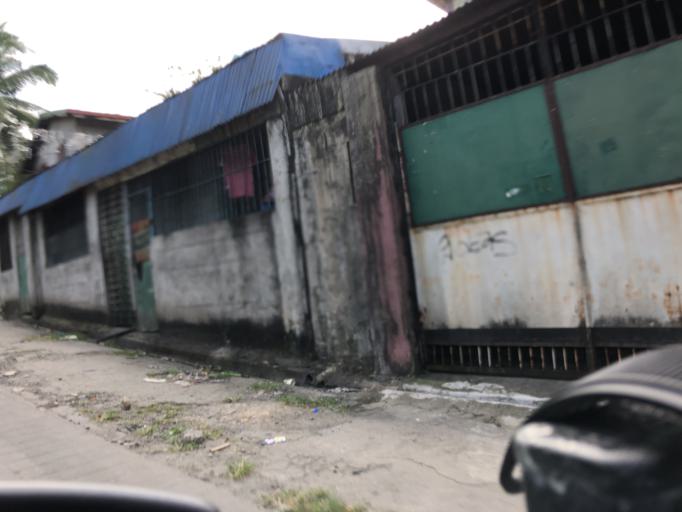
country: PH
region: Central Luzon
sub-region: Province of Bulacan
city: San Jose del Monte
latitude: 14.7428
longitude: 121.0605
